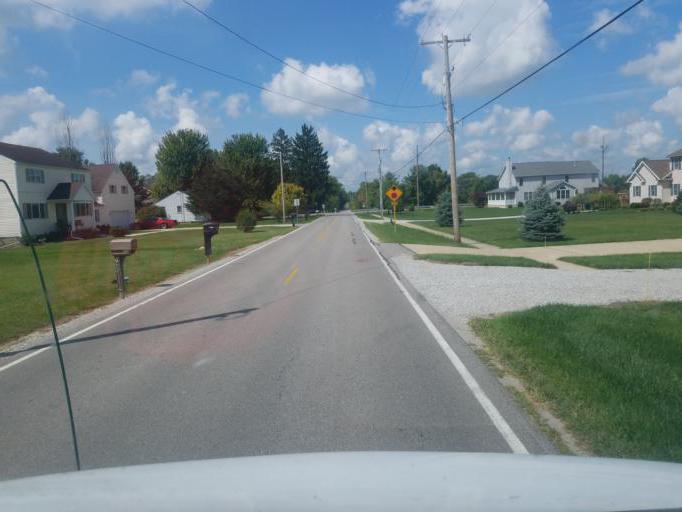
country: US
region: Ohio
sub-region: Marion County
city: Marion
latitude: 40.5202
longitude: -83.1493
